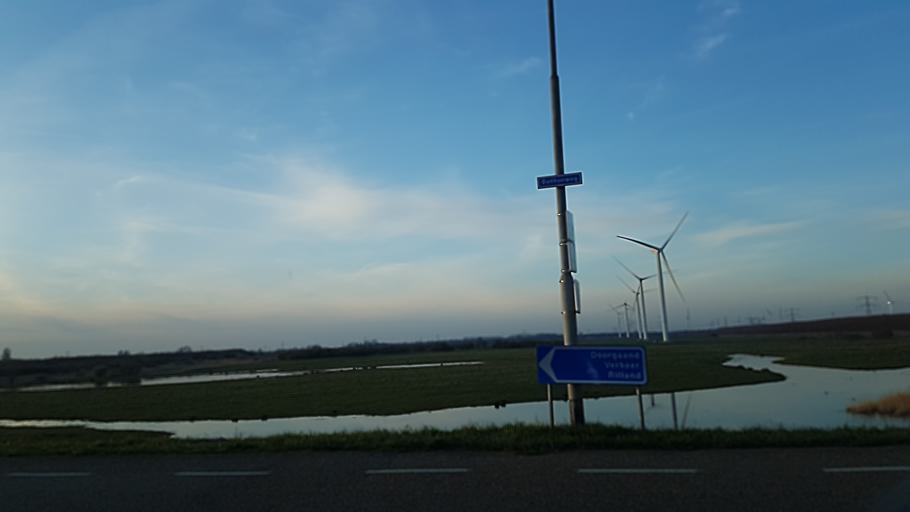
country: NL
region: North Brabant
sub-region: Gemeente Woensdrecht
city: Woensdrecht
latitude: 51.4018
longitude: 4.2315
